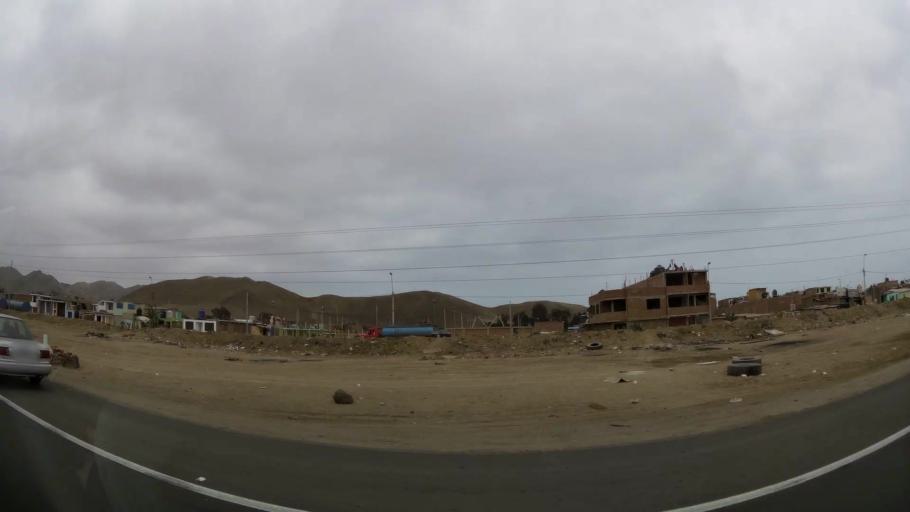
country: PE
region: Lima
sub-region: Lima
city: San Bartolo
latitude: -12.3892
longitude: -76.7662
